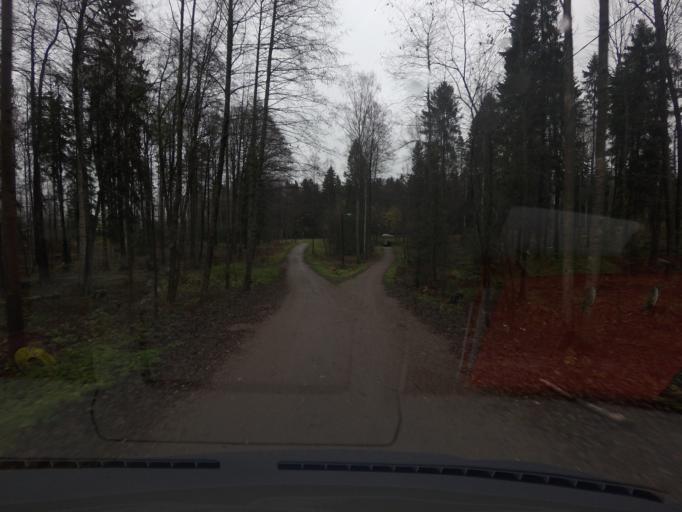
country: FI
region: Uusimaa
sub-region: Helsinki
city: Kauniainen
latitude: 60.2298
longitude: 24.7524
